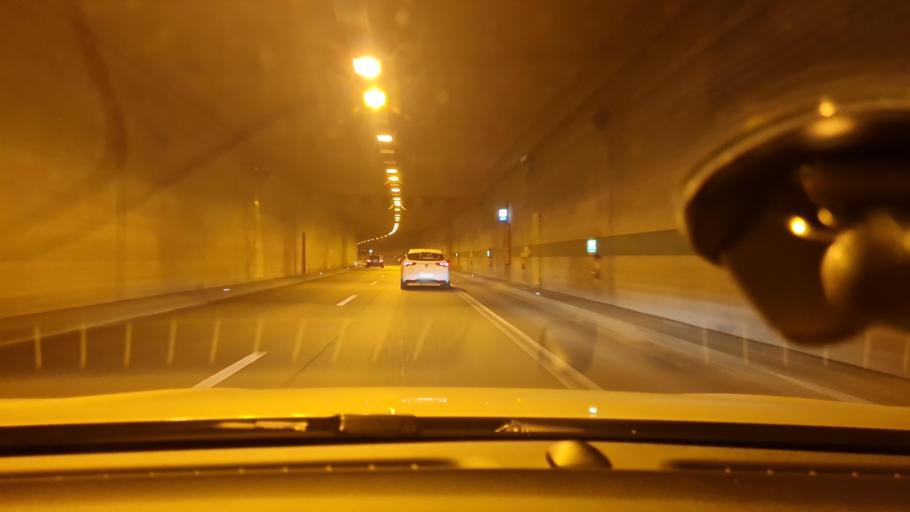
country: DE
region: North Rhine-Westphalia
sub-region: Regierungsbezirk Dusseldorf
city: Dusseldorf
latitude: 51.2297
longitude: 6.7709
